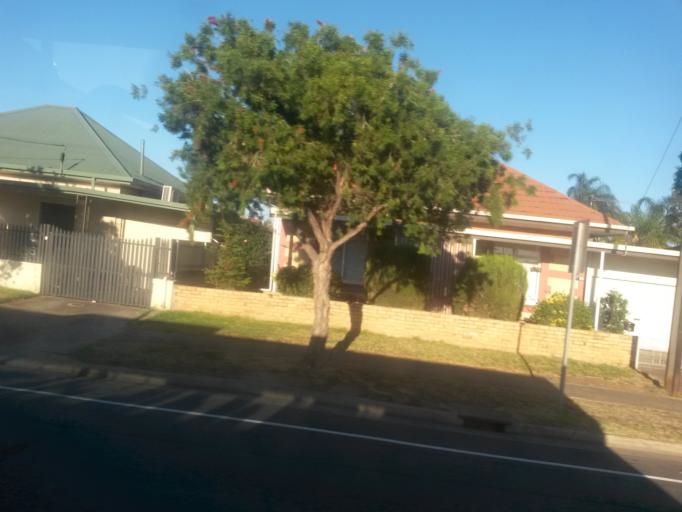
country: AU
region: South Australia
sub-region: Port Adelaide Enfield
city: Alberton
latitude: -34.8583
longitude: 138.5292
